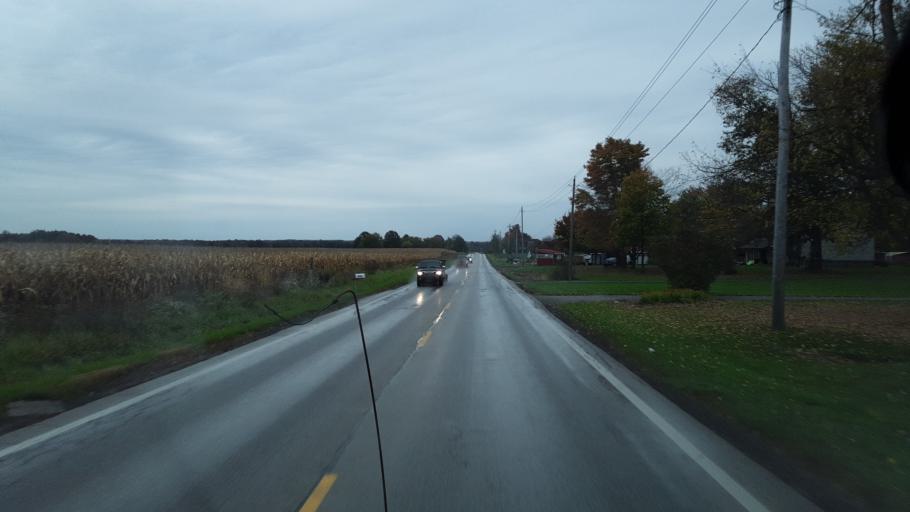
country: US
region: Ohio
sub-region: Ashtabula County
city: Orwell
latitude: 41.5353
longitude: -80.8374
